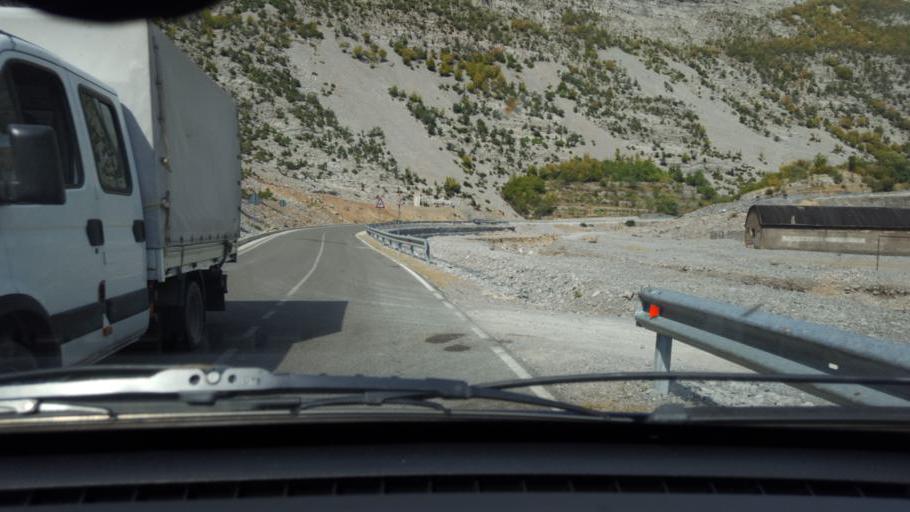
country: AL
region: Shkoder
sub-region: Rrethi i Malesia e Madhe
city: Kastrat
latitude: 42.4972
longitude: 19.5813
